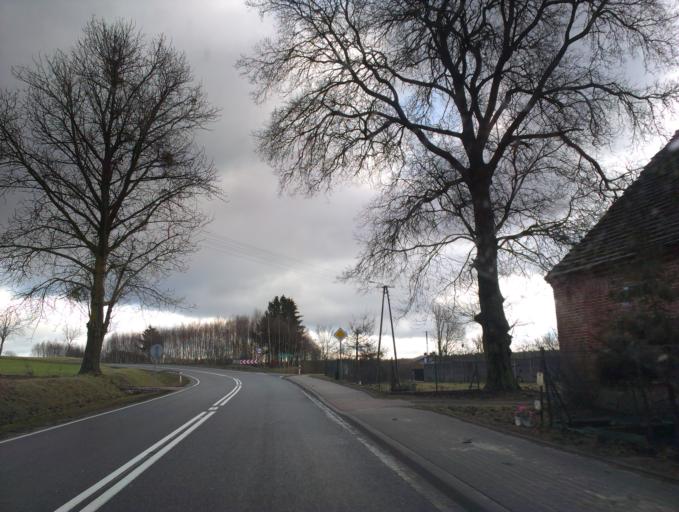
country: PL
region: Pomeranian Voivodeship
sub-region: Powiat czluchowski
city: Debrzno
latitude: 53.6255
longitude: 17.2351
